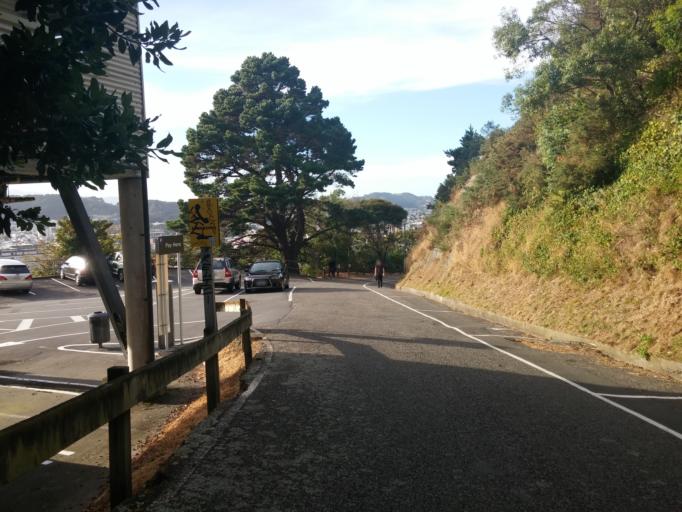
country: NZ
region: Wellington
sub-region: Wellington City
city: Wellington
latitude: -41.2908
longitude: 174.7690
